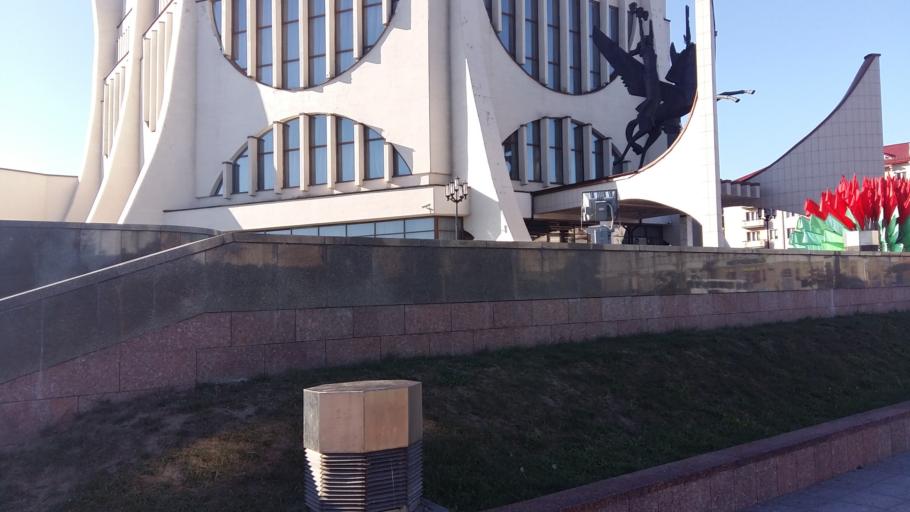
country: BY
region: Grodnenskaya
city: Hrodna
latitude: 53.6749
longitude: 23.8282
